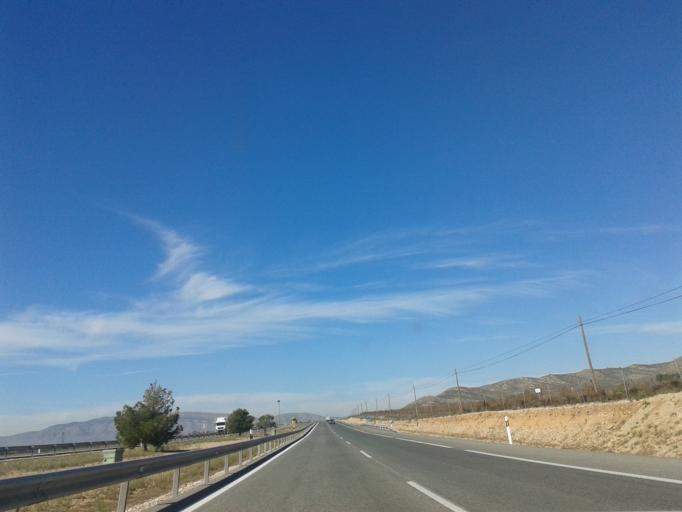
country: ES
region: Valencia
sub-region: Provincia de Alicante
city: Villena
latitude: 38.6777
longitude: -0.8946
